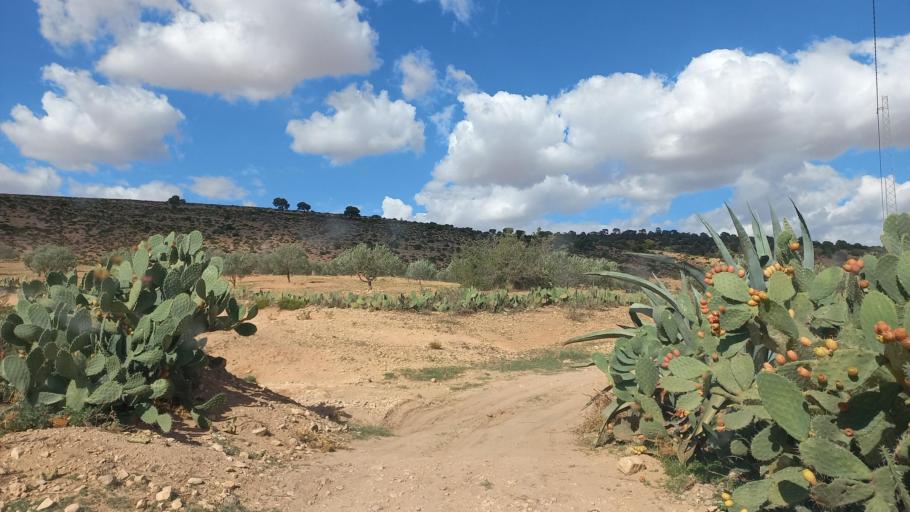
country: TN
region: Al Qasrayn
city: Kasserine
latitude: 35.3727
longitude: 8.8836
